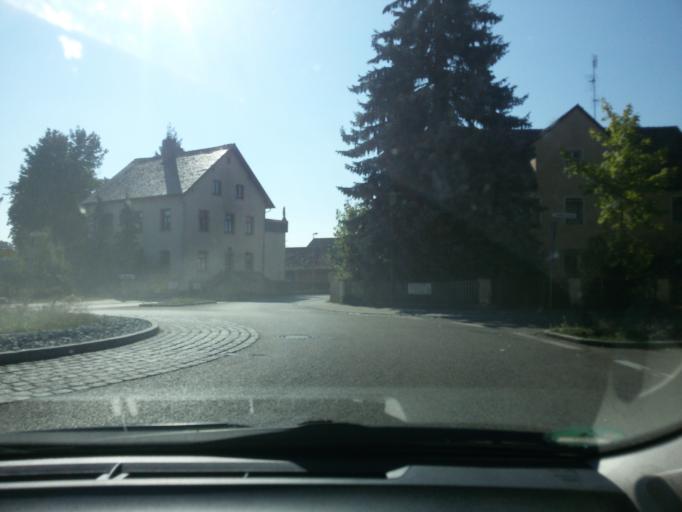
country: DE
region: Bavaria
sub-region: Regierungsbezirk Mittelfranken
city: Wassertrudingen
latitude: 49.0429
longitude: 10.6048
